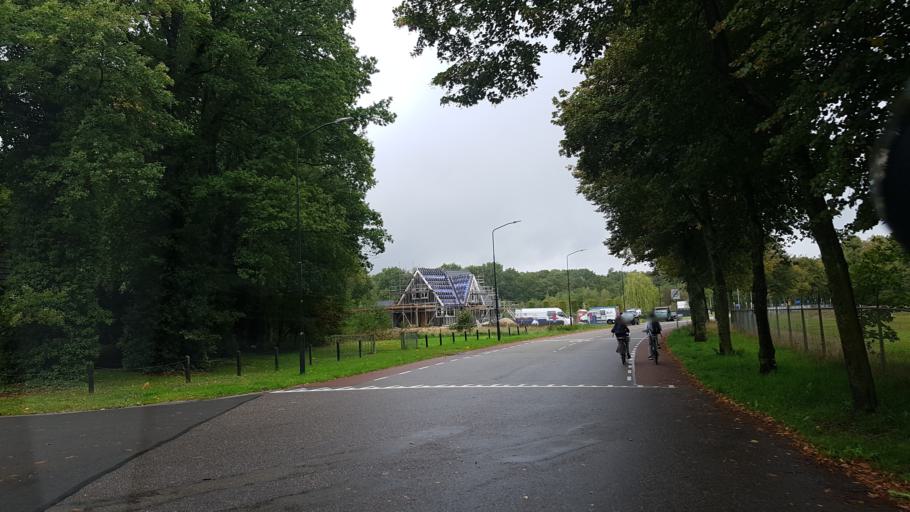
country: NL
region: Gelderland
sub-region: Gemeente Apeldoorn
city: Beekbergen
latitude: 52.1885
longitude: 5.9308
